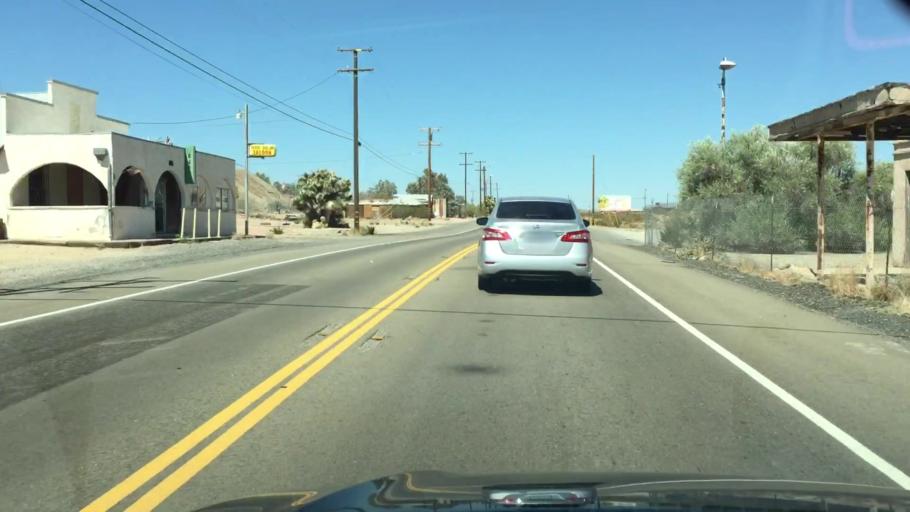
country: US
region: California
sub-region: Kern County
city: Ridgecrest
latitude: 35.3546
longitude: -117.6181
